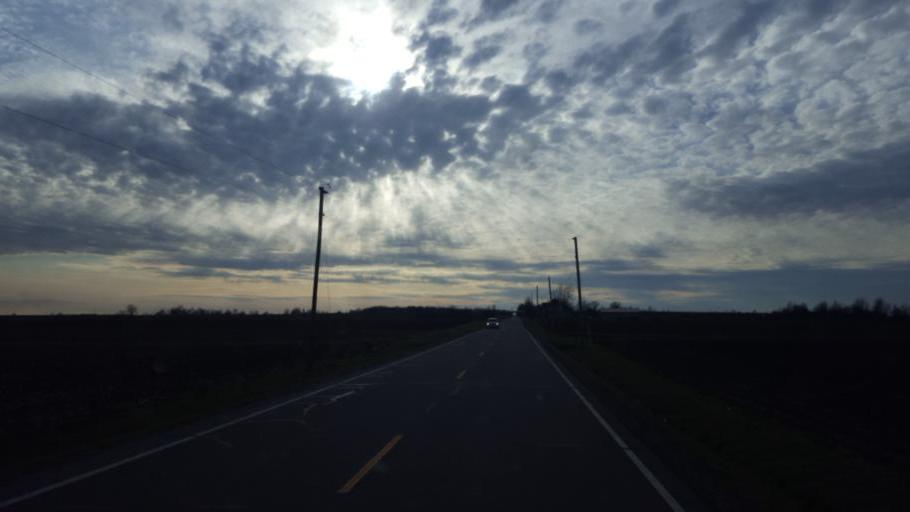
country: US
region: Ohio
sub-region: Crawford County
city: Bucyrus
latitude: 40.7983
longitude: -82.9081
